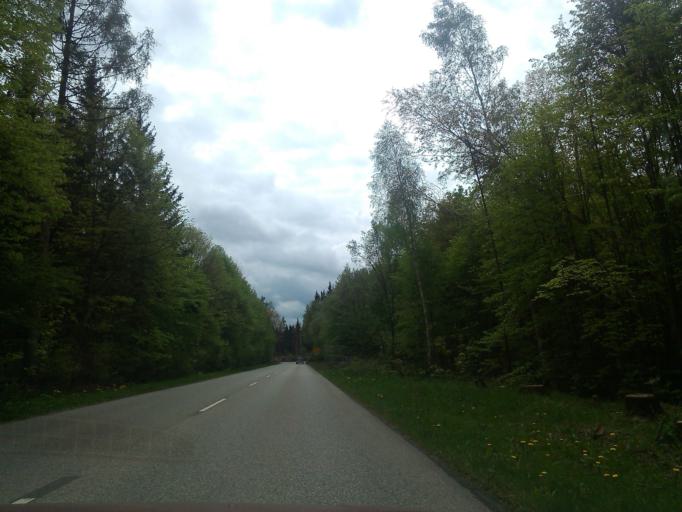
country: DE
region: Bavaria
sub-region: Upper Bavaria
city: Krailling
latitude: 48.0999
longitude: 11.3740
